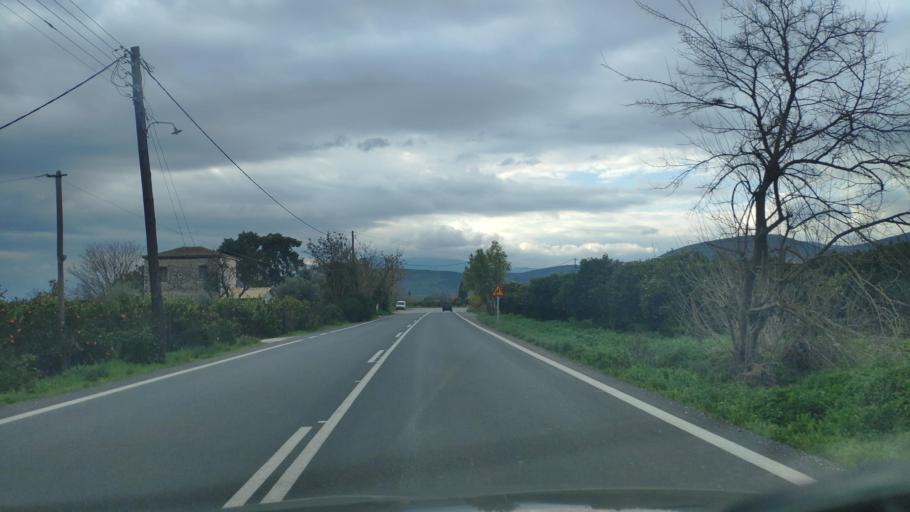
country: GR
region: Peloponnese
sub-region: Nomos Argolidos
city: Nea Kios
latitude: 37.5798
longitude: 22.7093
